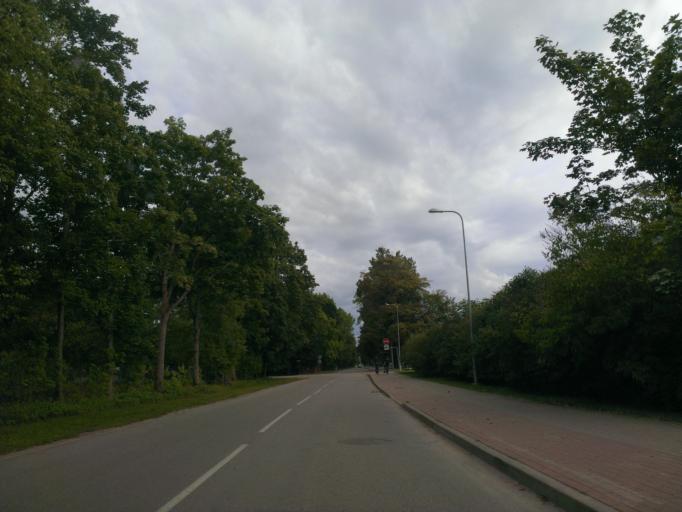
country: LV
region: Ikskile
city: Ikskile
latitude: 56.8304
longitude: 24.4873
